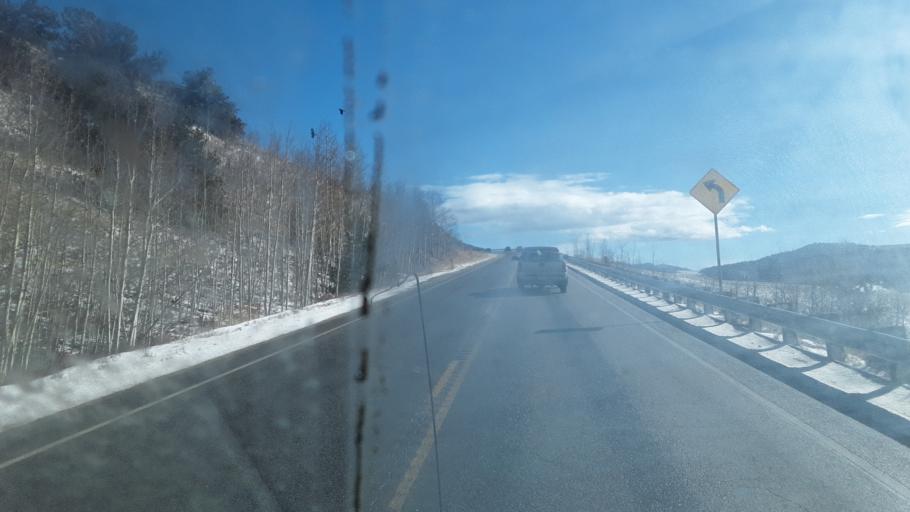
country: US
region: Colorado
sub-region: Summit County
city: Breckenridge
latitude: 39.4038
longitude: -105.7654
